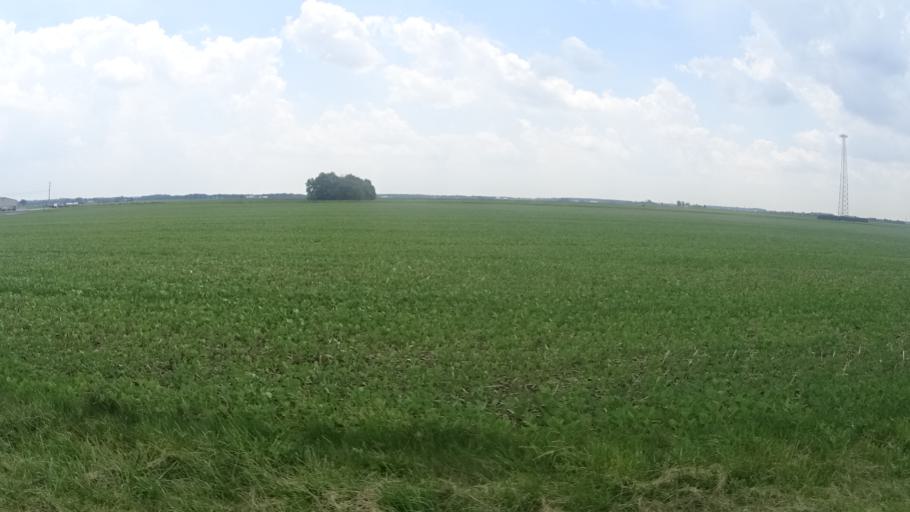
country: US
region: Ohio
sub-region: Huron County
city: Monroeville
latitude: 41.3104
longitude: -82.6870
